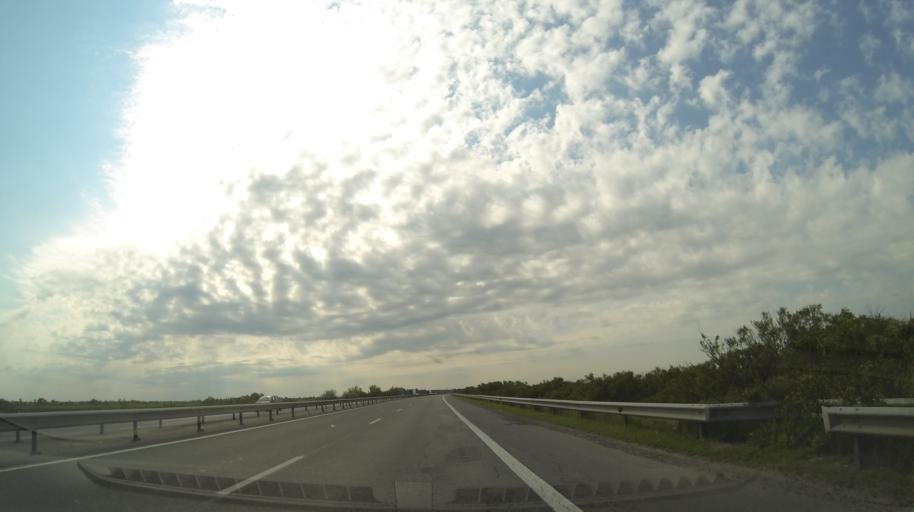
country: RO
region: Arges
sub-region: Comuna Cateasca
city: Cateasca
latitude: 44.7492
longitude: 25.0963
